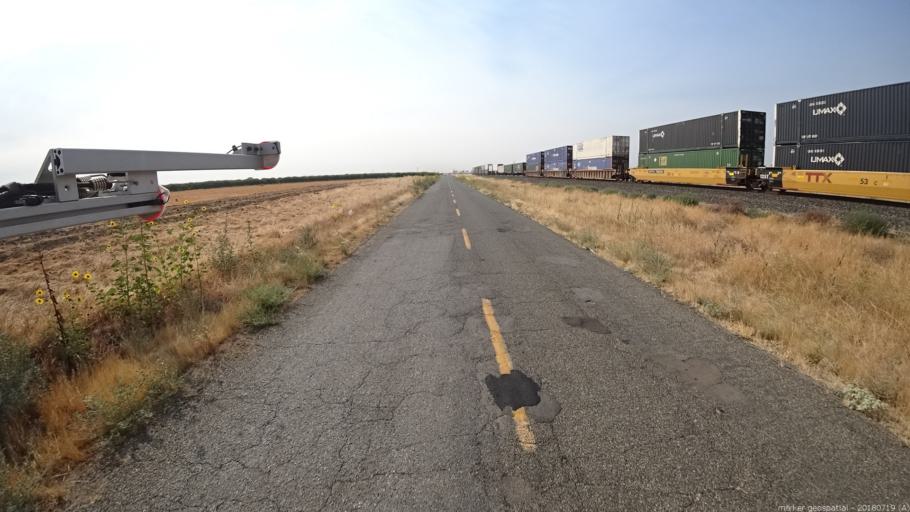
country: US
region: California
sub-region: Madera County
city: Fairmead
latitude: 37.0576
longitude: -120.1746
